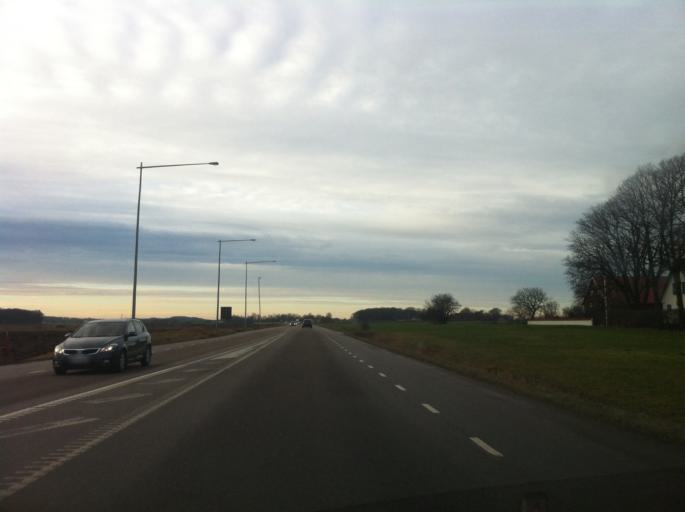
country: SE
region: Skane
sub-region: Helsingborg
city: Hyllinge
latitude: 56.1010
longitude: 12.8440
